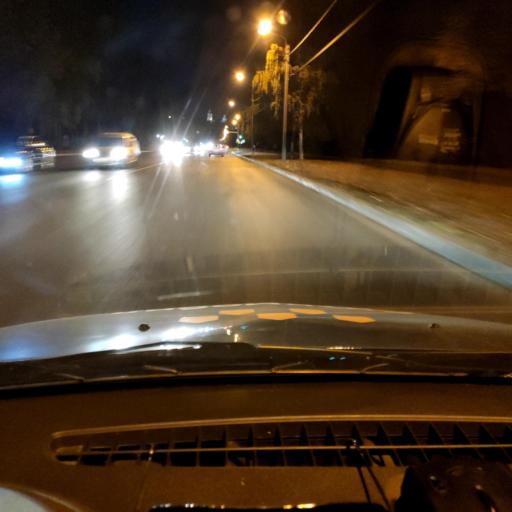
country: RU
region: Voronezj
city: Voronezh
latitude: 51.6492
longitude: 39.2115
